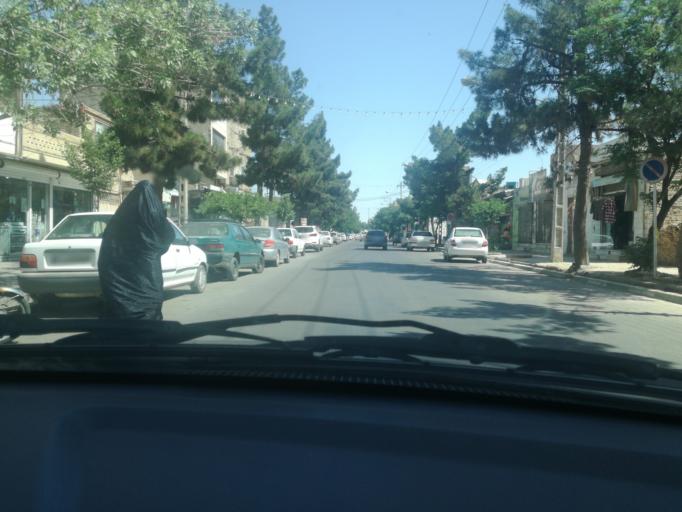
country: IR
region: Razavi Khorasan
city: Sarakhs
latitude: 36.5387
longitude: 61.1635
